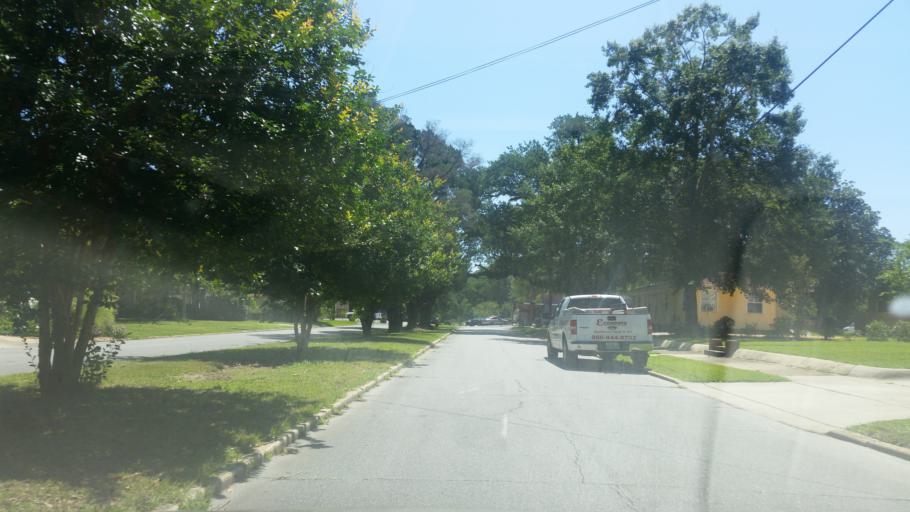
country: US
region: Florida
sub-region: Escambia County
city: Goulding
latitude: 30.4359
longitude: -87.2064
